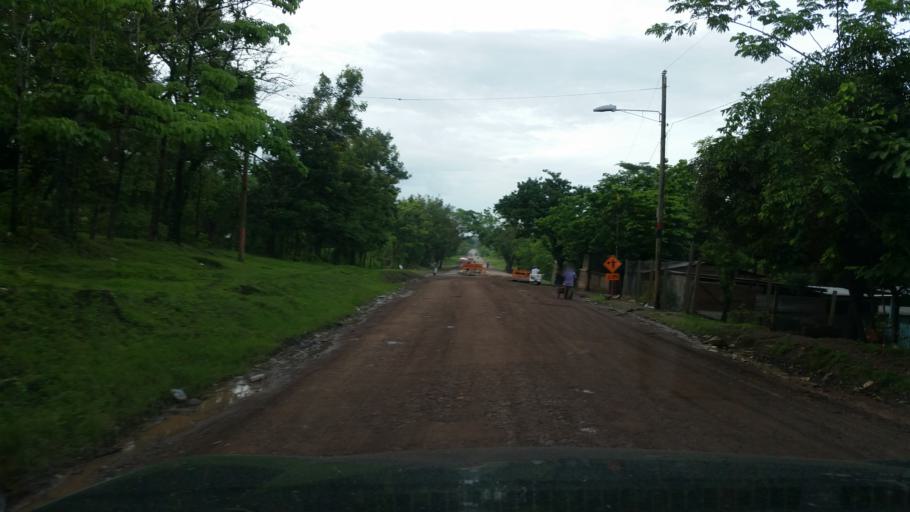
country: NI
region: Matagalpa
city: Rio Blanco
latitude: 13.1853
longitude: -84.9507
